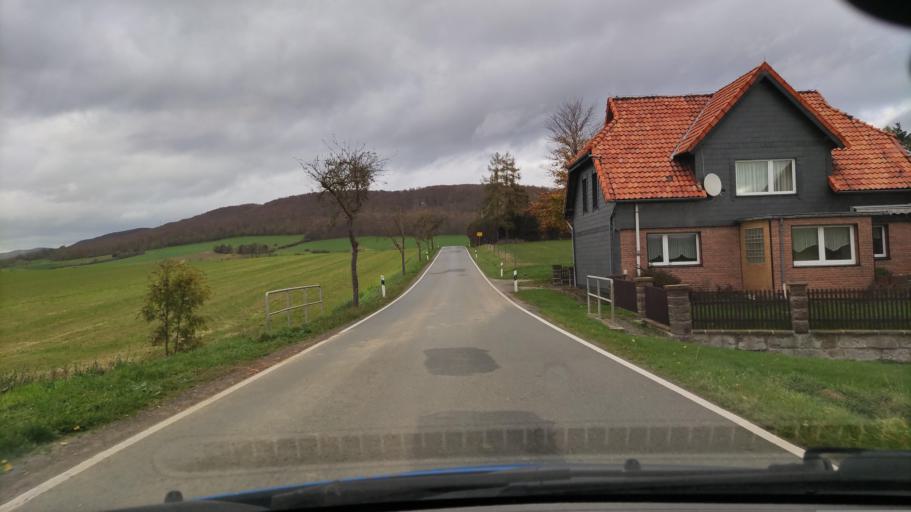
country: DE
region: Lower Saxony
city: Holzen
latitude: 51.9293
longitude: 9.6660
